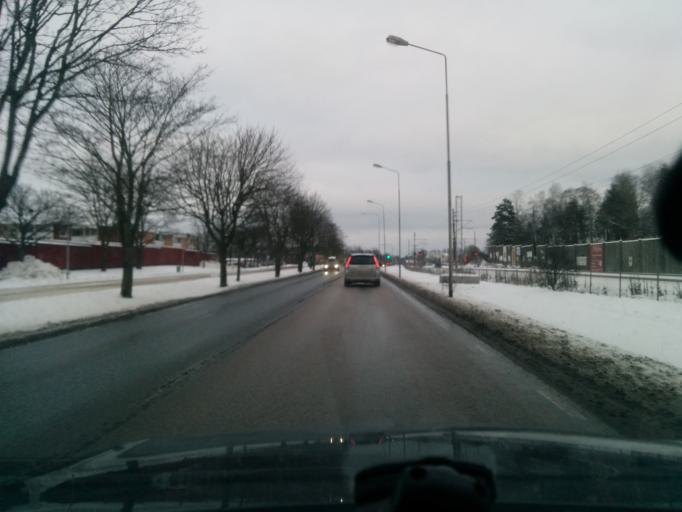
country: SE
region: Stockholm
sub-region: Taby Kommun
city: Taby
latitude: 59.4461
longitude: 18.0799
